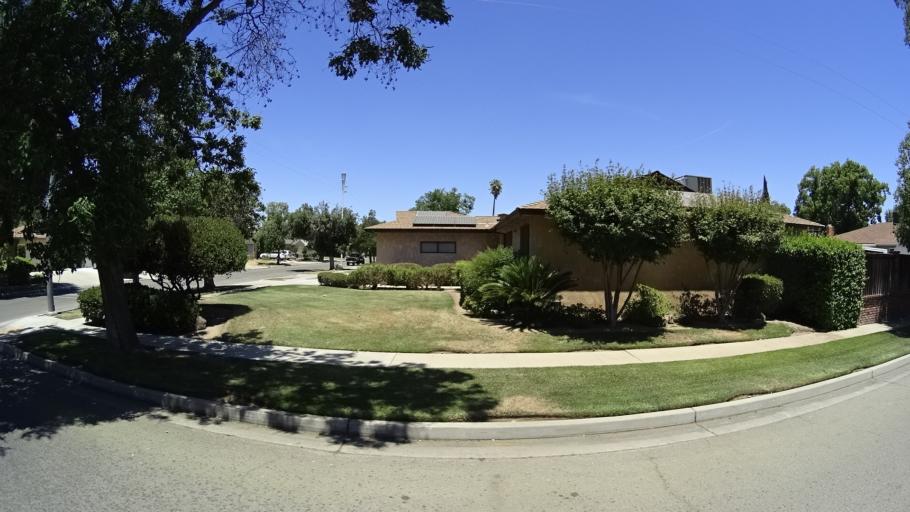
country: US
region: California
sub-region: Fresno County
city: Tarpey Village
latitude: 36.7981
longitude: -119.7485
